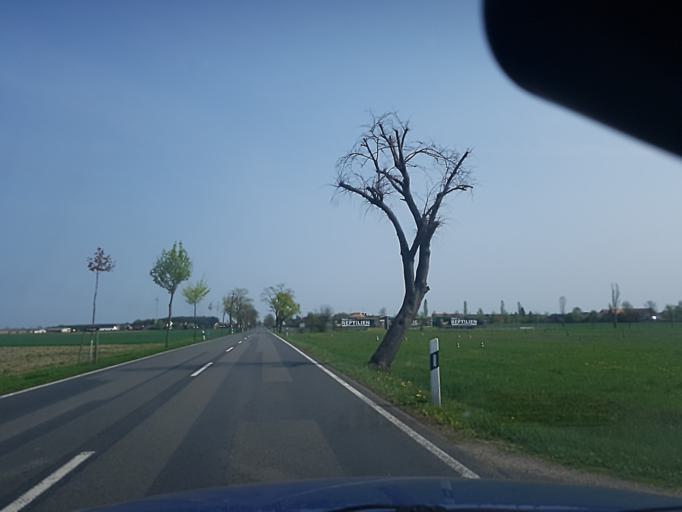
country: DE
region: Saxony
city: Beilrode
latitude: 51.5948
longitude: 13.1201
